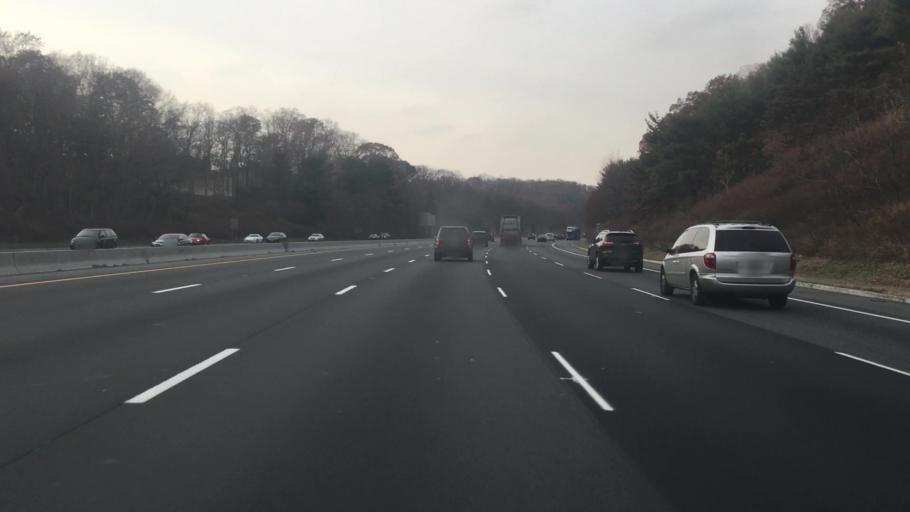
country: US
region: New Jersey
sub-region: Morris County
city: Parsippany
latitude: 40.8690
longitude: -74.4581
